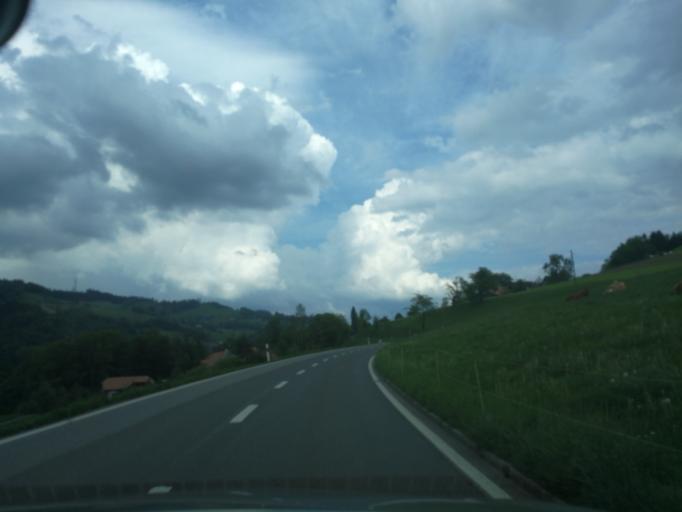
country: CH
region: Lucerne
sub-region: Entlebuch District
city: Oberdiessbach
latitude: 46.8351
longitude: 7.6376
